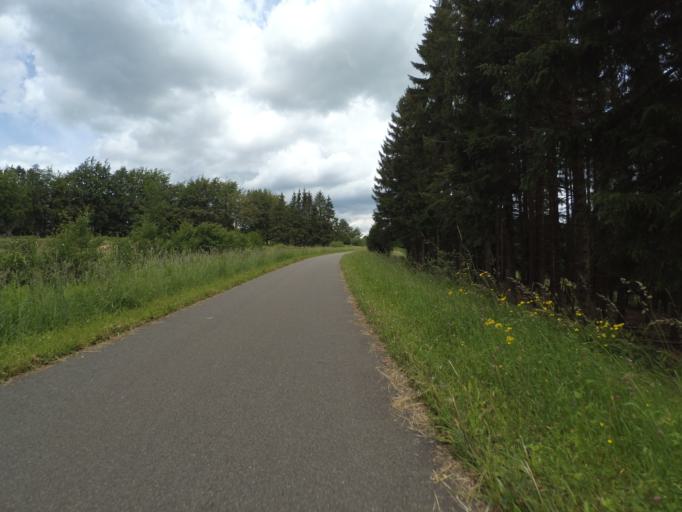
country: DE
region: North Rhine-Westphalia
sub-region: Regierungsbezirk Koln
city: Monschau
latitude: 50.5726
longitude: 6.2364
